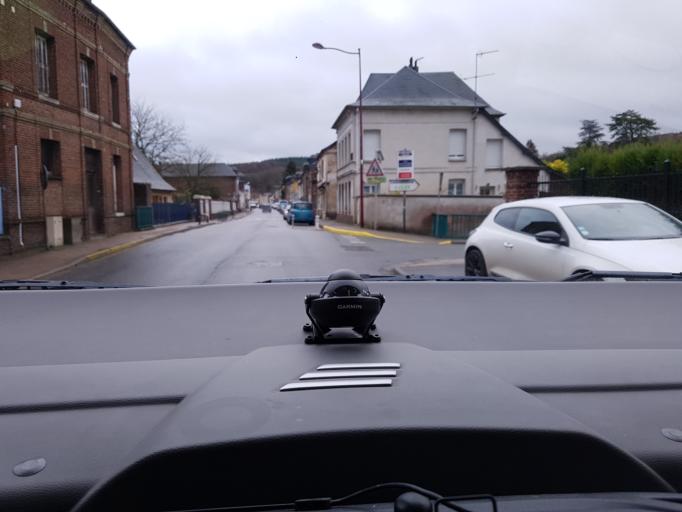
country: FR
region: Haute-Normandie
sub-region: Departement de l'Eure
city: Pont-Saint-Pierre
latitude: 49.3338
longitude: 1.2747
